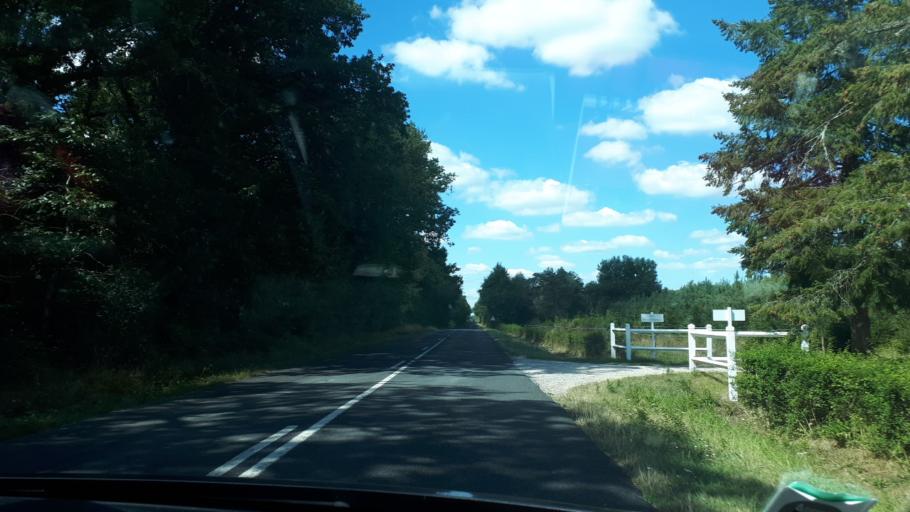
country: FR
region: Centre
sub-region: Departement du Loir-et-Cher
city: Dhuizon
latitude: 47.5343
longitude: 1.7171
